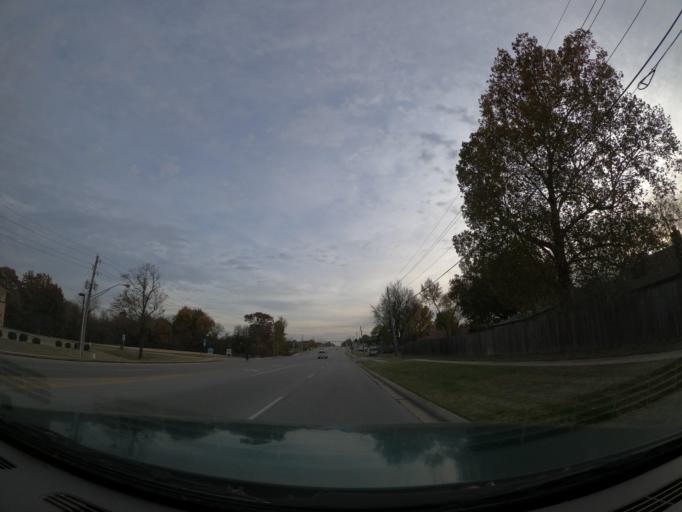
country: US
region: Oklahoma
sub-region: Tulsa County
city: Broken Arrow
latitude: 36.0495
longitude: -95.8154
